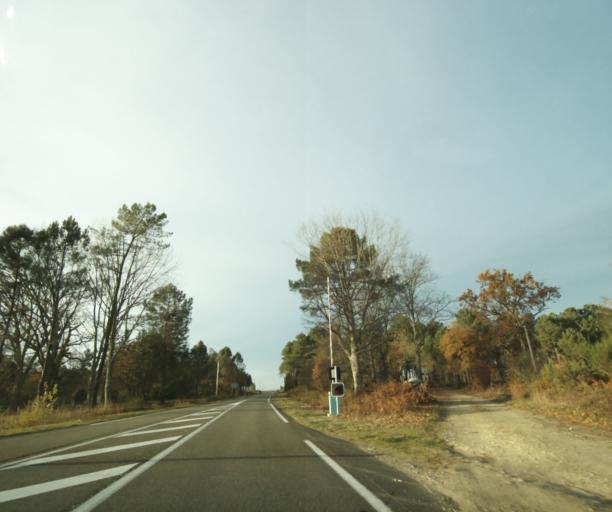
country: FR
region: Aquitaine
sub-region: Departement des Landes
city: Gabarret
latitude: 44.0685
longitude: -0.0602
